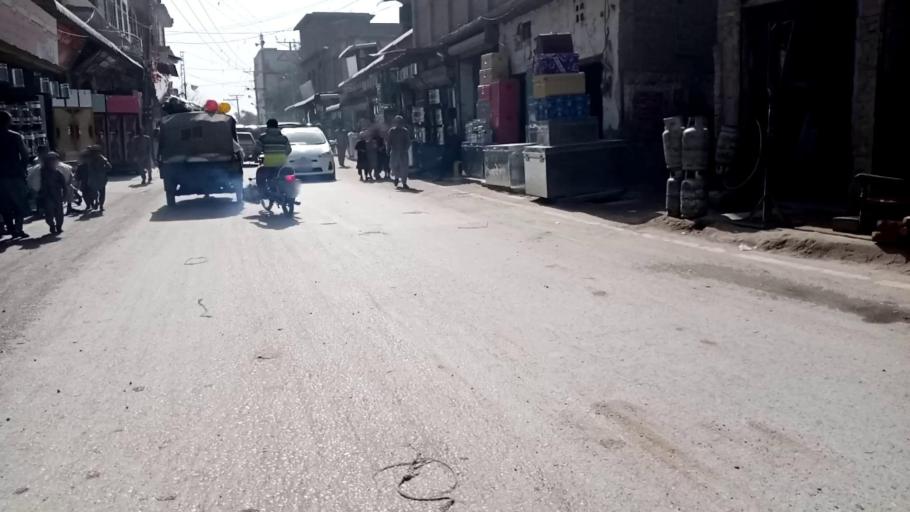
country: PK
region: Khyber Pakhtunkhwa
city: Peshawar
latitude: 34.0020
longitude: 71.5859
